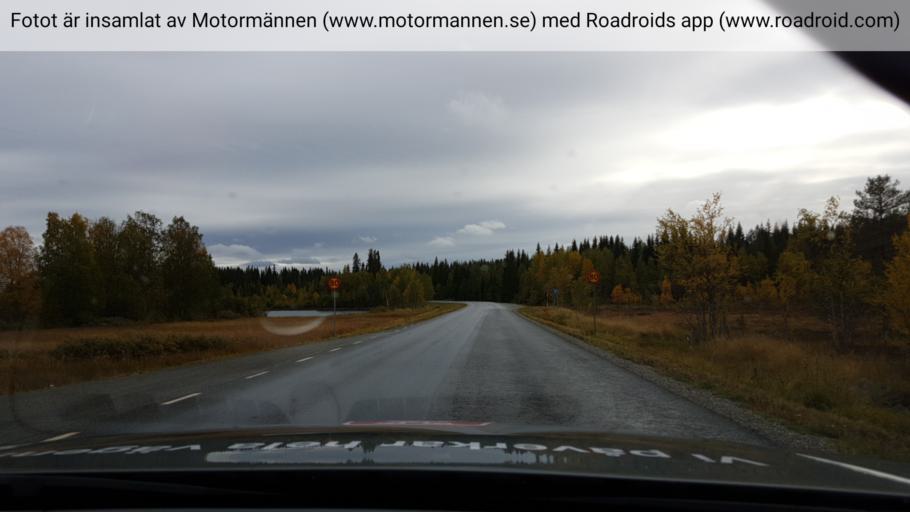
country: SE
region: Vaesterbotten
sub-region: Vilhelmina Kommun
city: Sjoberg
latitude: 64.6748
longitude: 16.2925
